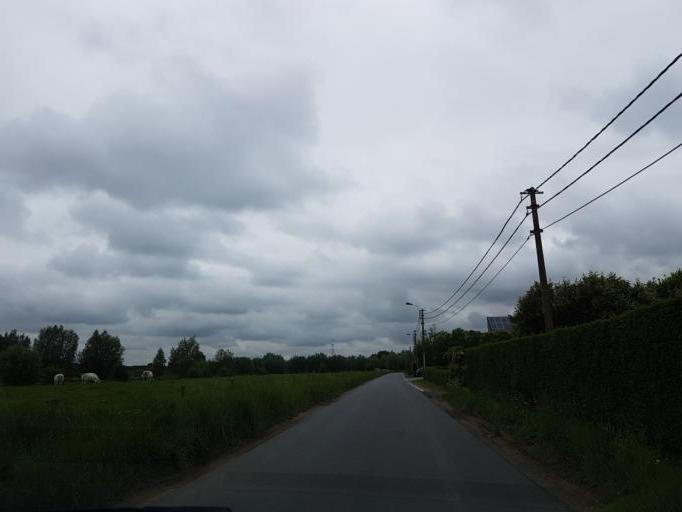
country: BE
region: Flanders
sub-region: Provincie Oost-Vlaanderen
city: Lovendegem
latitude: 51.0891
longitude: 3.5862
